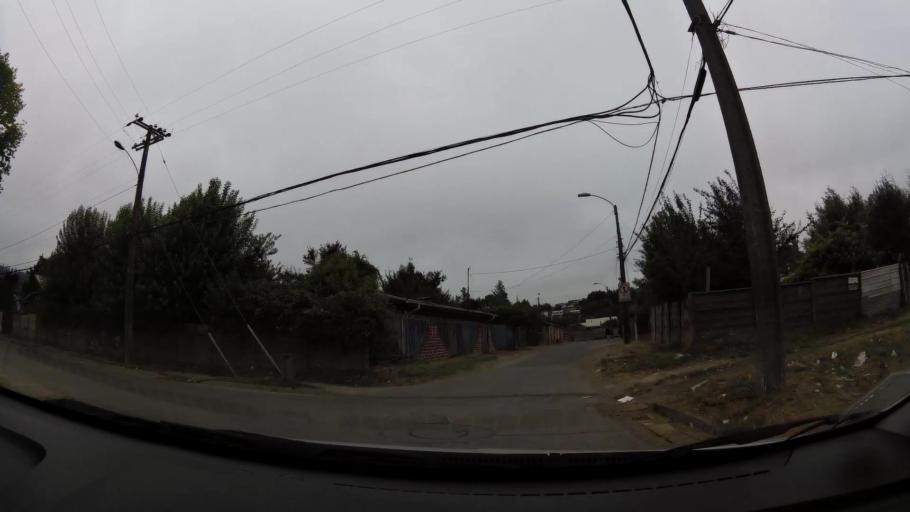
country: CL
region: Biobio
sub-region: Provincia de Concepcion
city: Concepcion
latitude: -36.8325
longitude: -73.0071
